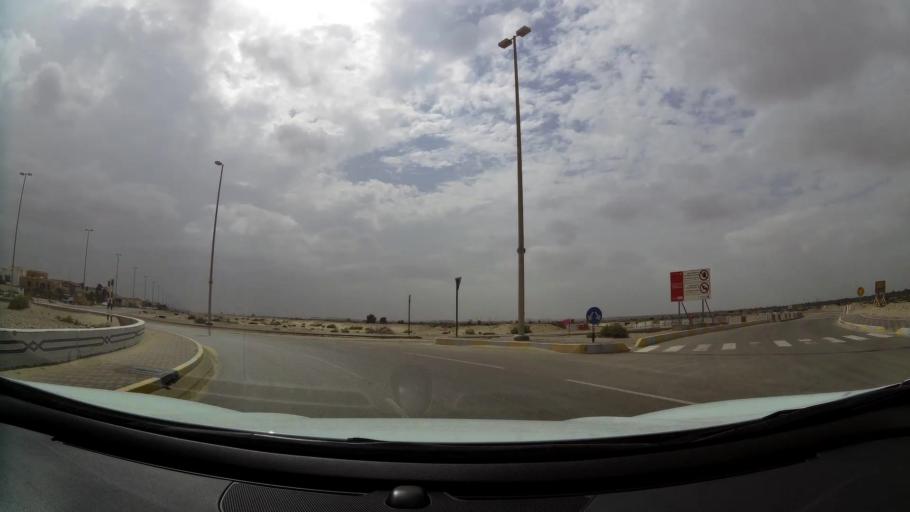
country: AE
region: Abu Dhabi
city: Abu Dhabi
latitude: 24.4034
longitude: 54.6521
